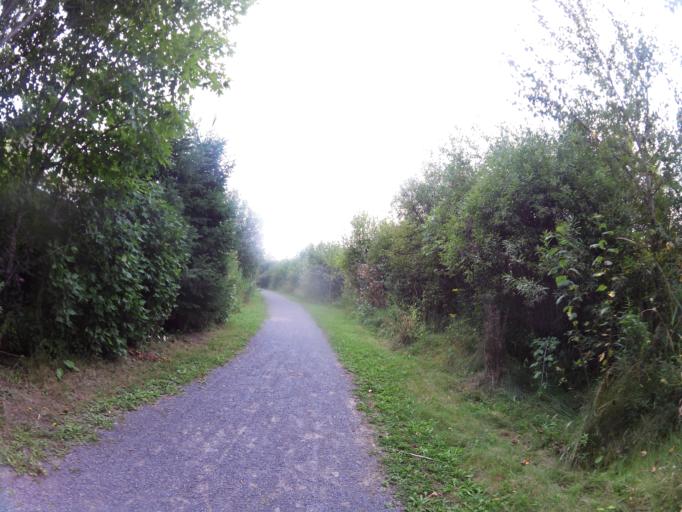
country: CA
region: Ontario
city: Bells Corners
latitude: 45.2783
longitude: -75.9345
